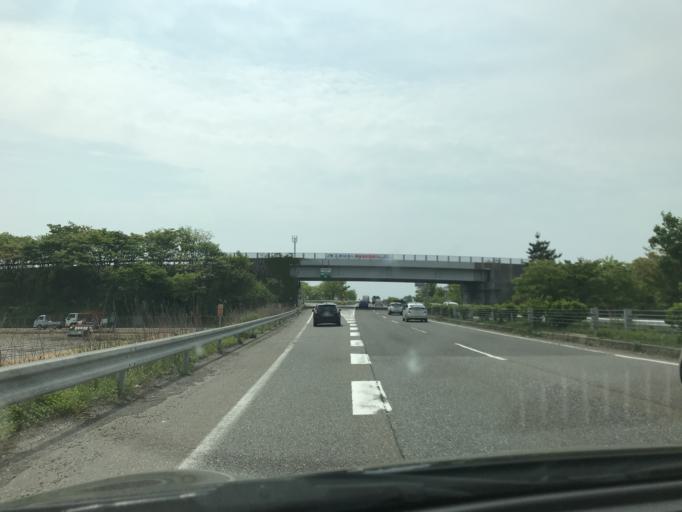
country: JP
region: Niigata
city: Kameda-honcho
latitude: 37.8804
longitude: 139.0820
